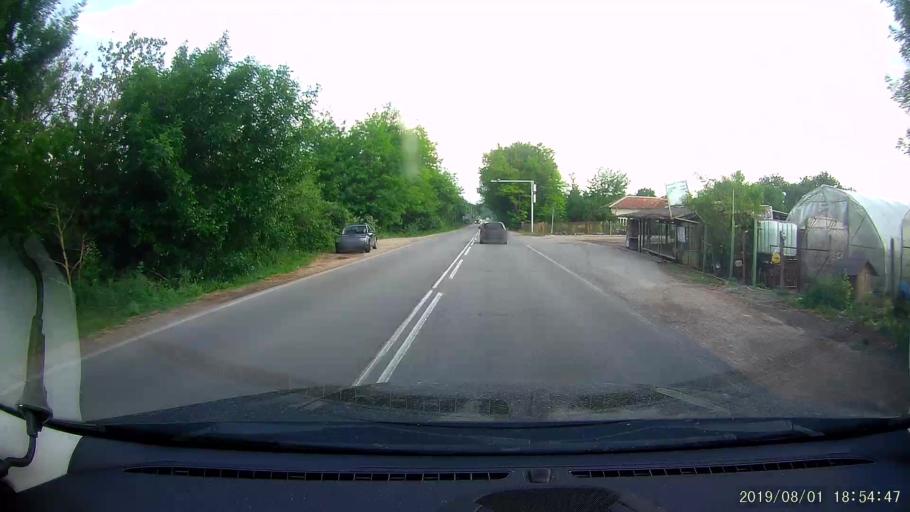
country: BG
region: Shumen
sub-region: Obshtina Shumen
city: Shumen
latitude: 43.1908
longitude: 27.0032
